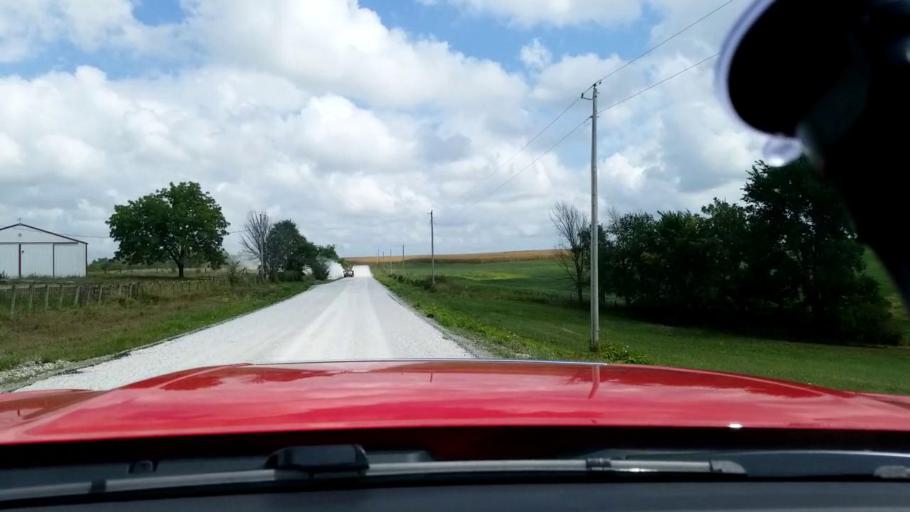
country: US
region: Iowa
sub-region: Decatur County
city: Lamoni
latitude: 40.6548
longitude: -94.0514
